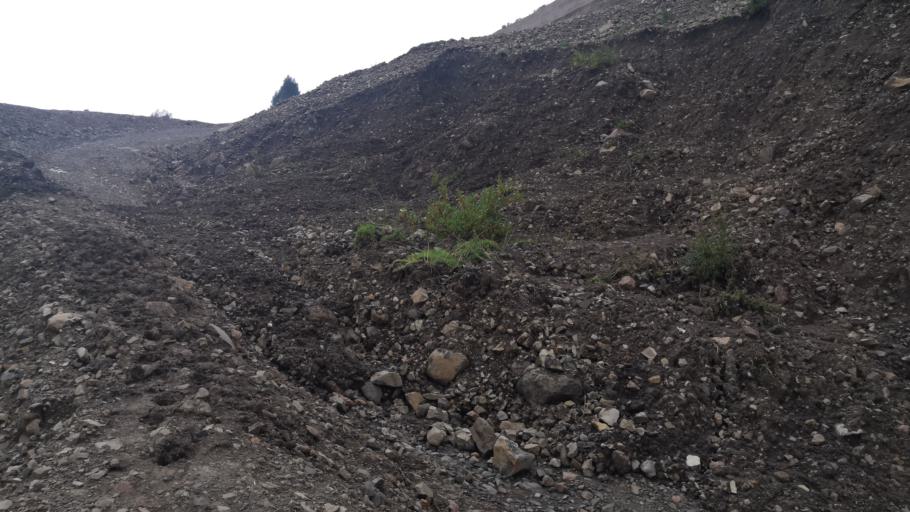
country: ET
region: Amhara
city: Kemise
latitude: 10.3376
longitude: 39.8201
